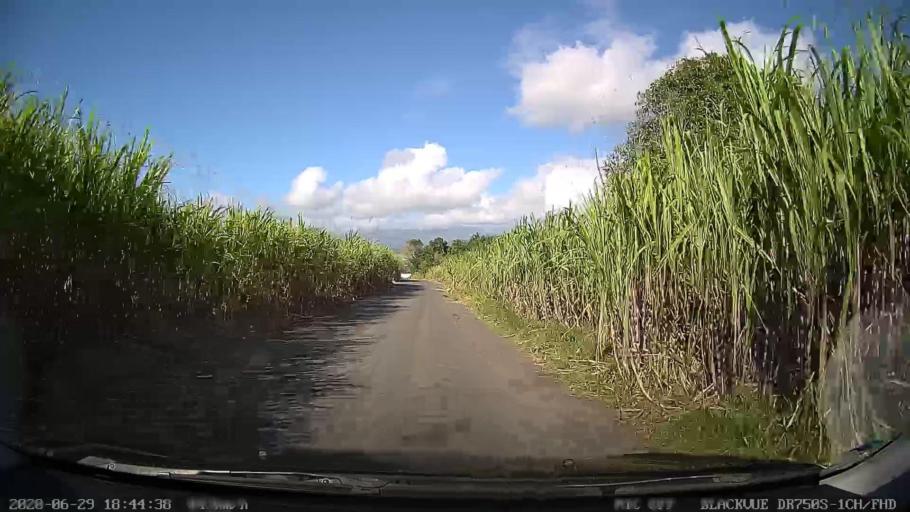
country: RE
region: Reunion
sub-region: Reunion
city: Bras-Panon
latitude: -20.9958
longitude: 55.6857
